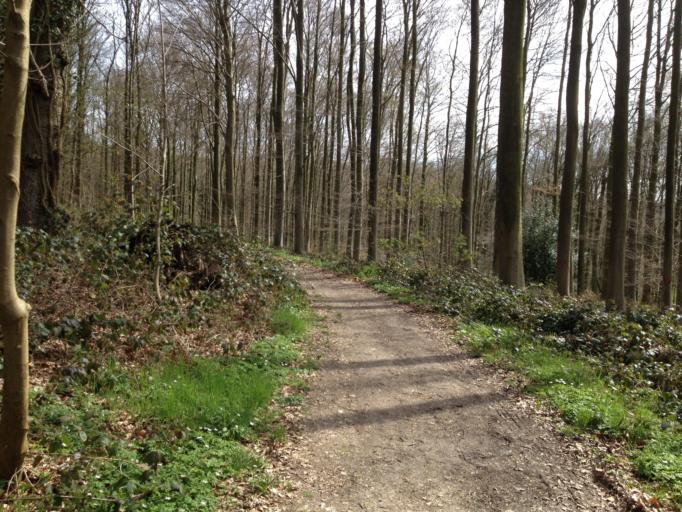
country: BE
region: Flanders
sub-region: Provincie Limburg
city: Sint-Pieters-Voeren
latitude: 50.7764
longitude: 5.8601
